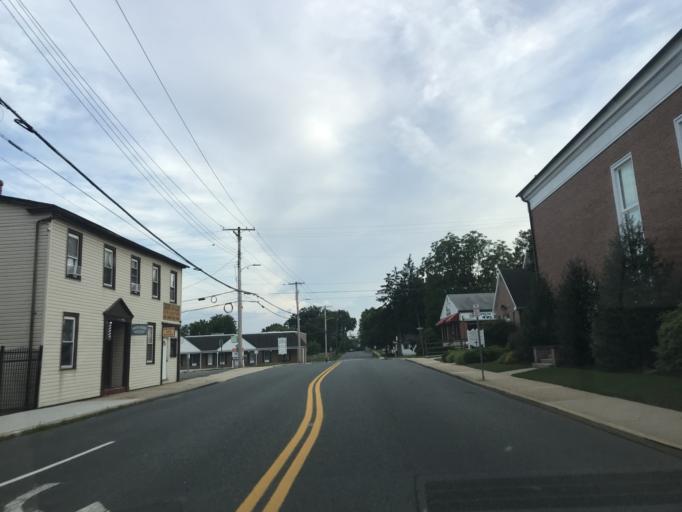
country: US
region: Maryland
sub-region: Harford County
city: Aberdeen
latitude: 39.5098
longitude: -76.1655
